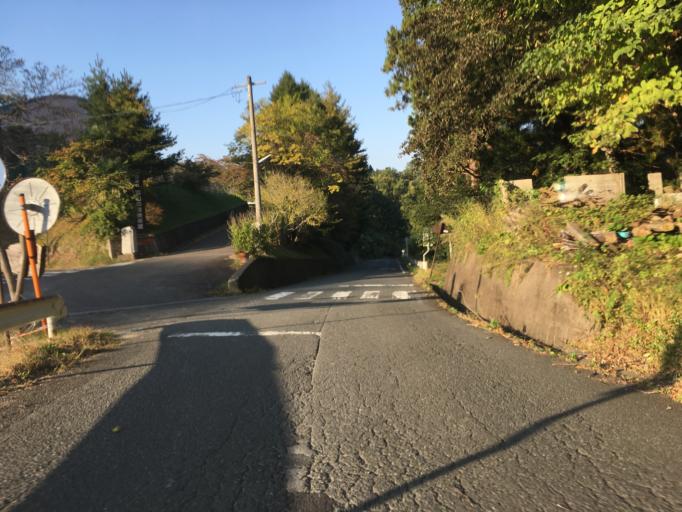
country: JP
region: Fukushima
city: Fukushima-shi
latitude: 37.6497
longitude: 140.5804
